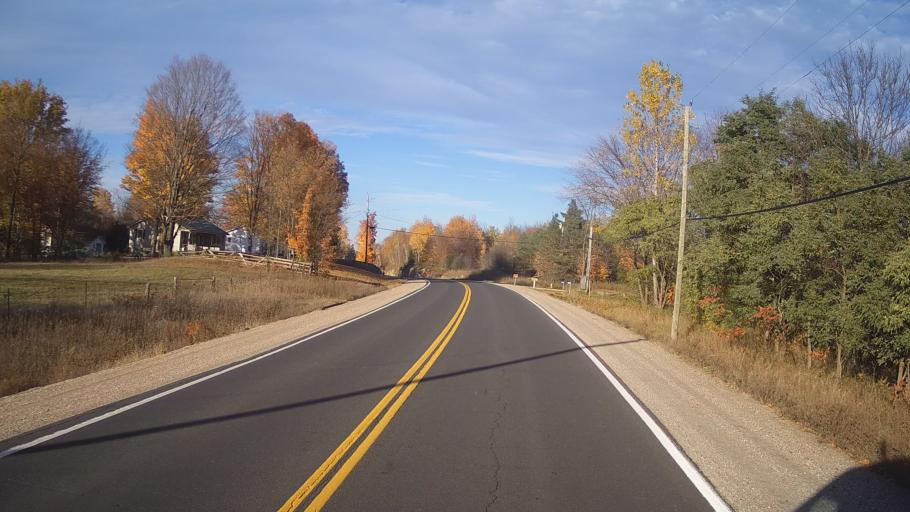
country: CA
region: Ontario
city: Perth
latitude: 44.8040
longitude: -76.3321
